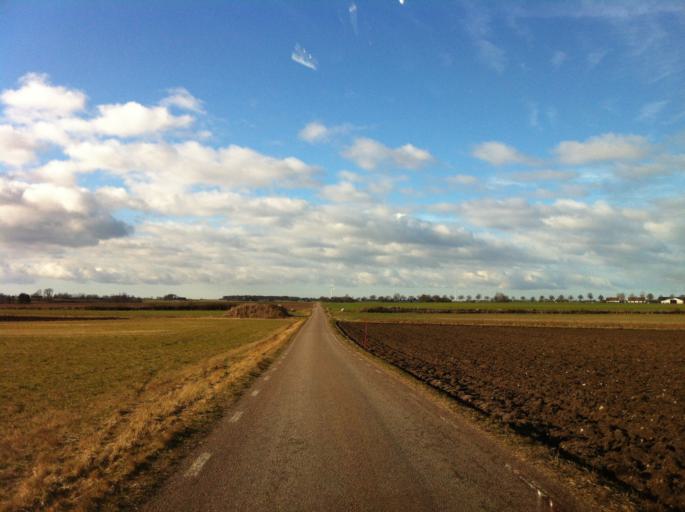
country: SE
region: Skane
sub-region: Landskrona
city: Asmundtorp
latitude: 55.9331
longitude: 13.0080
